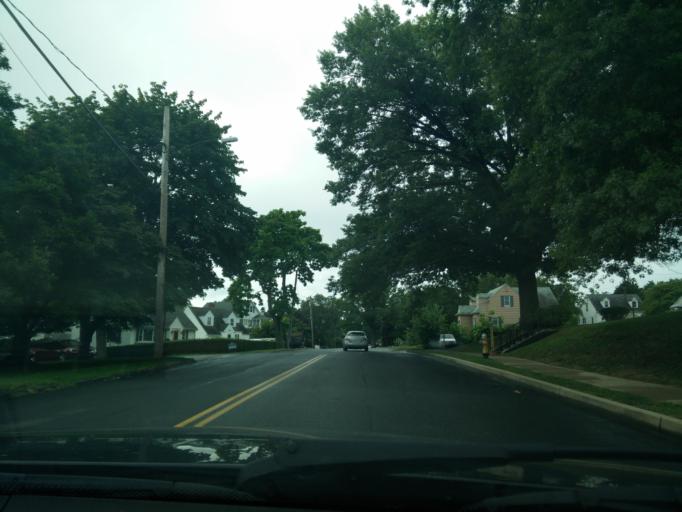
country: US
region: Connecticut
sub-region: Fairfield County
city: Bridgeport
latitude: 41.1789
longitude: -73.2325
